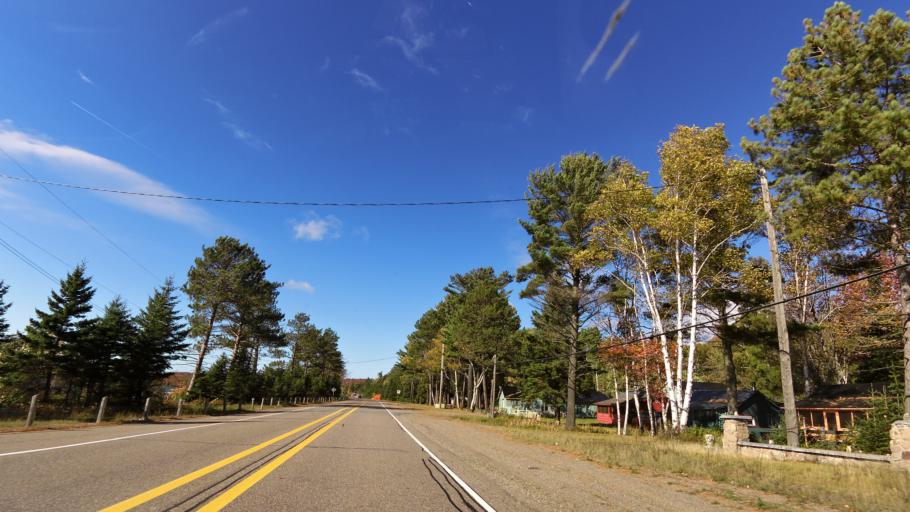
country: CA
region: Ontario
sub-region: Algoma
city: Sault Ste. Marie
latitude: 46.9458
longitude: -84.5663
